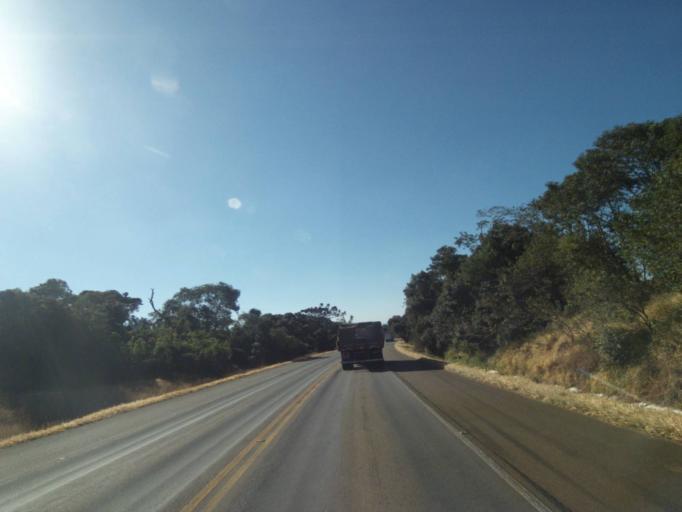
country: BR
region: Parana
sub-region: Tibagi
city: Tibagi
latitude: -24.6677
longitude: -50.4530
